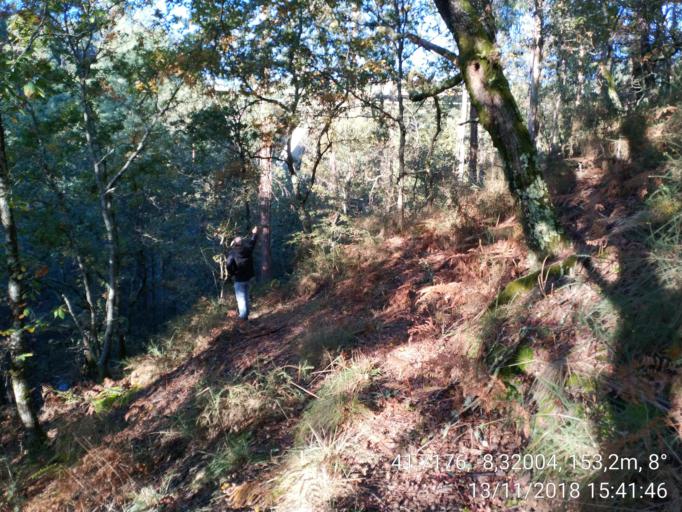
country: PT
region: Braga
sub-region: Terras de Bouro
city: Terras de Bouro
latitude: 41.7176
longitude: -8.3200
